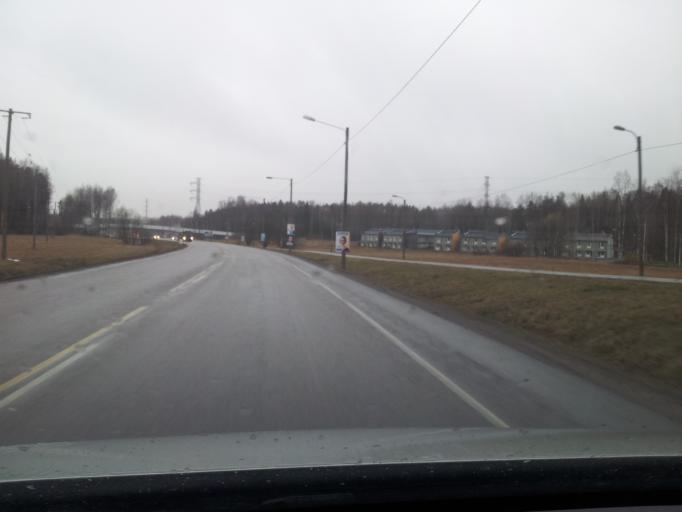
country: FI
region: Uusimaa
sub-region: Helsinki
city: Espoo
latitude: 60.1654
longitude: 24.6254
